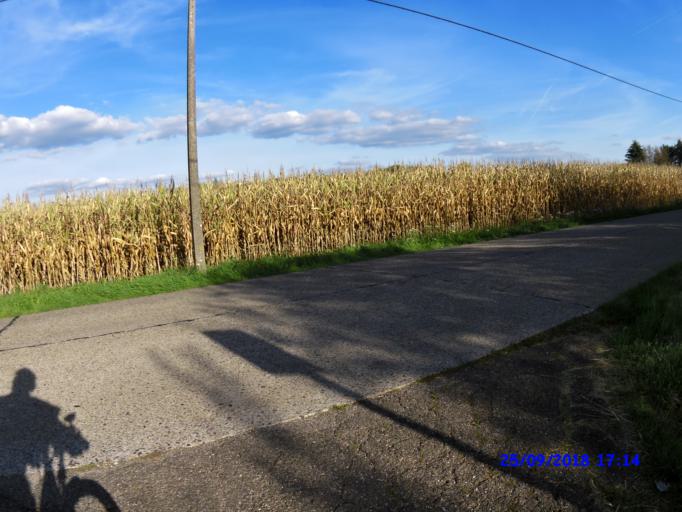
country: BE
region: Flanders
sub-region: Provincie Vlaams-Brabant
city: Begijnendijk
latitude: 51.0358
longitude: 4.7920
